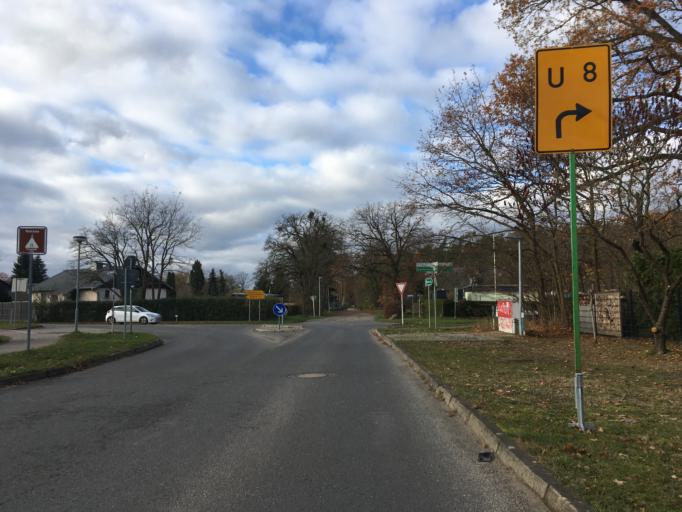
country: DE
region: Brandenburg
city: Rehfelde
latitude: 52.5348
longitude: 13.9353
